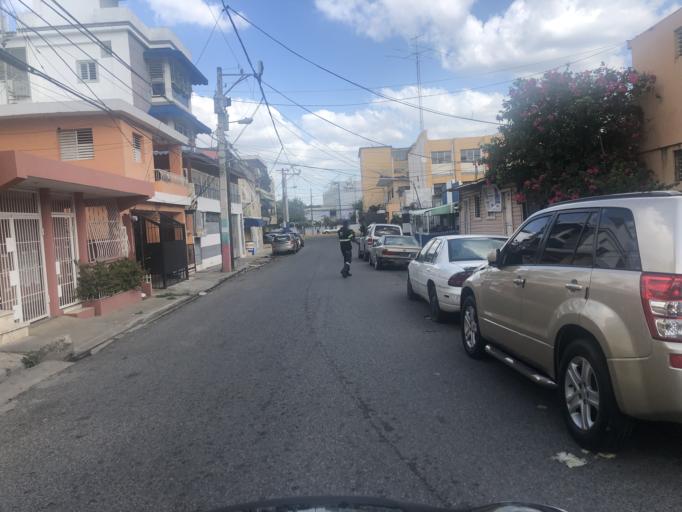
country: DO
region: Nacional
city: La Julia
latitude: 18.4563
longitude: -69.9263
